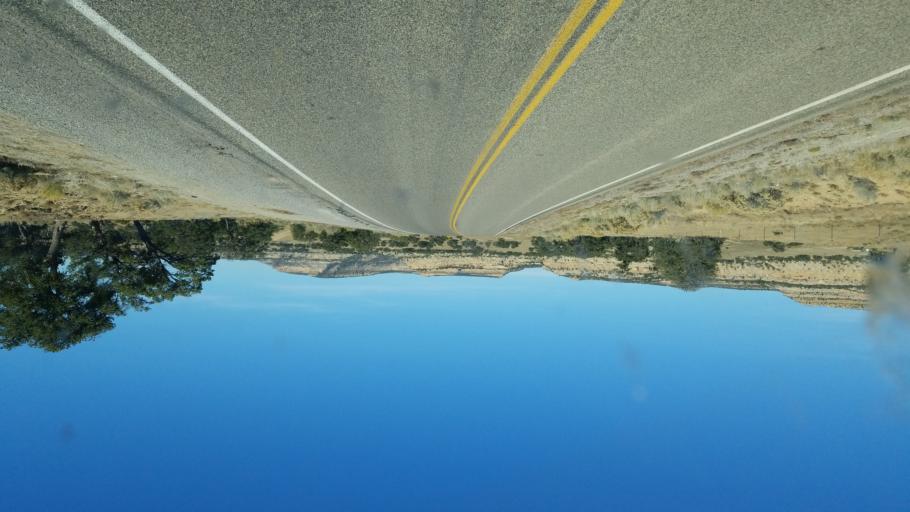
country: US
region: New Mexico
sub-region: McKinley County
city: Crownpoint
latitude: 35.5585
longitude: -108.1131
